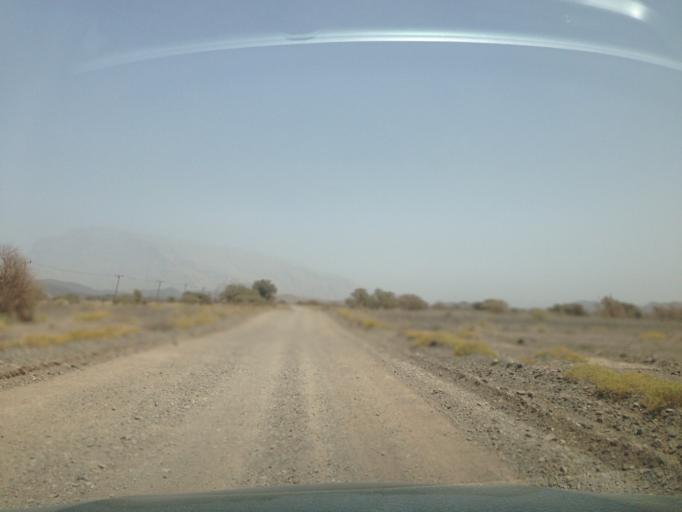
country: OM
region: Az Zahirah
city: `Ibri
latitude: 23.2204
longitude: 56.8261
